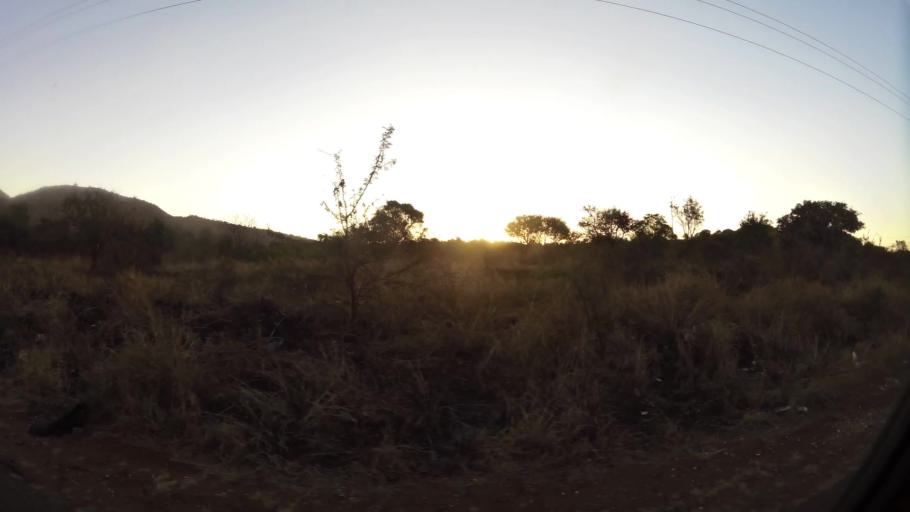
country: ZA
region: North-West
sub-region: Bojanala Platinum District Municipality
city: Rustenburg
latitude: -25.6348
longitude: 27.2017
